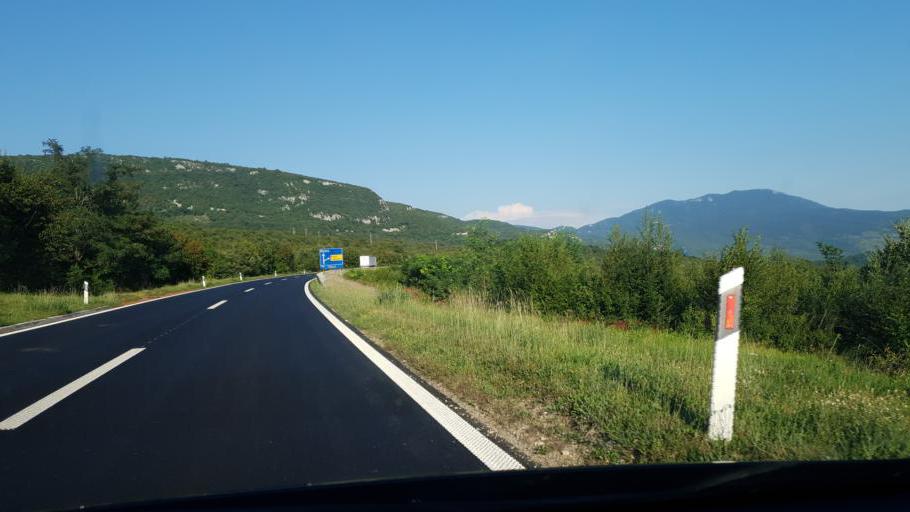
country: HR
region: Istarska
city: Buzet
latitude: 45.3507
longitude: 14.0966
